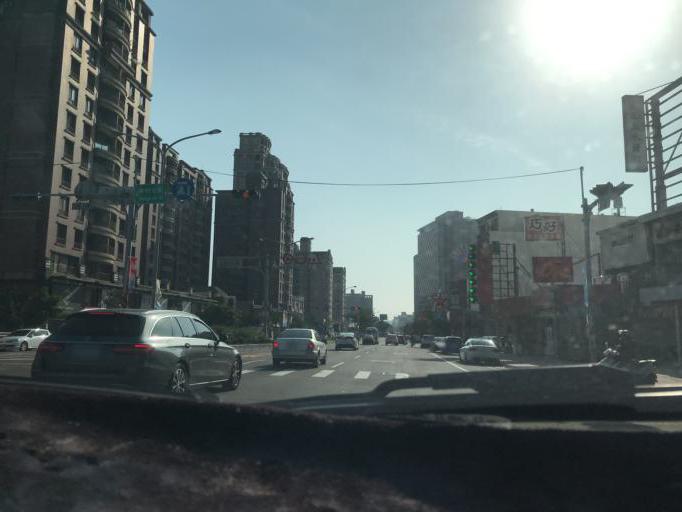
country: TW
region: Taiwan
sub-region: Hsinchu
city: Zhubei
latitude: 24.8237
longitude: 121.0313
